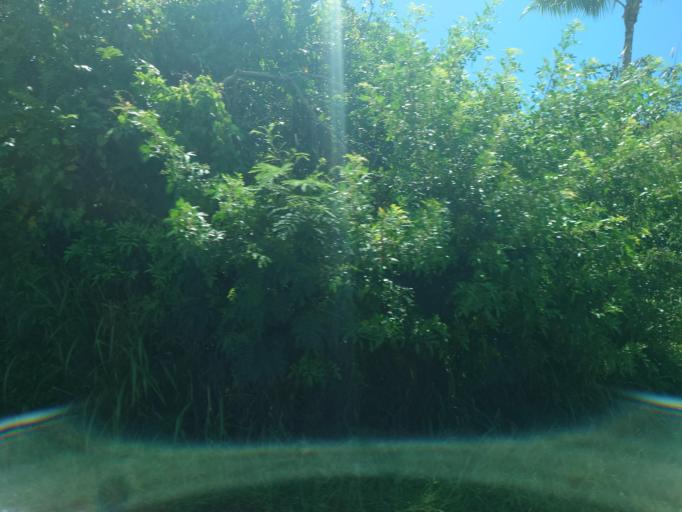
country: NC
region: South Province
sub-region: Noumea
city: Noumea
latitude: -22.2742
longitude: 166.4494
